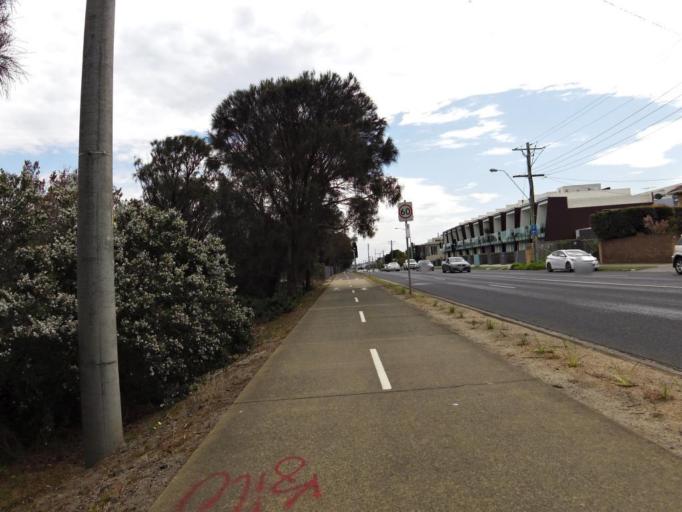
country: AU
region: Victoria
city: Hampton
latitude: -37.9587
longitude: 145.0095
